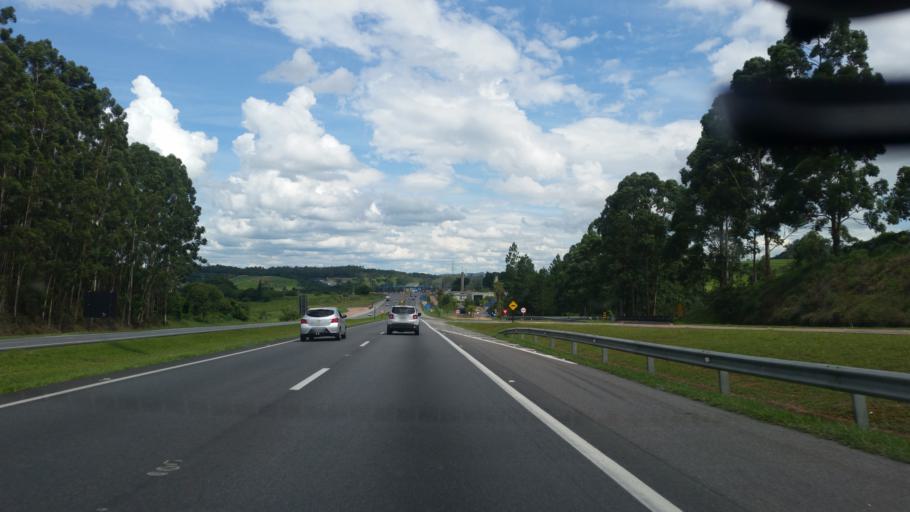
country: BR
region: Sao Paulo
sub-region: Itatiba
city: Itatiba
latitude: -22.9493
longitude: -46.8673
